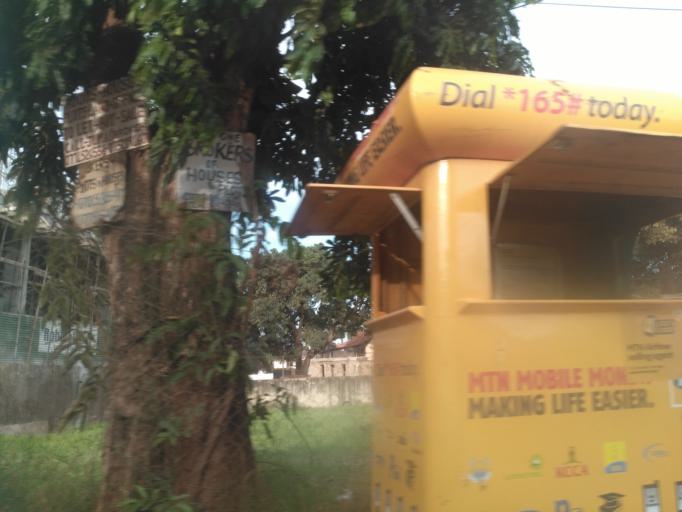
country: UG
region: Central Region
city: Kampala Central Division
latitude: 0.3389
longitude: 32.5853
